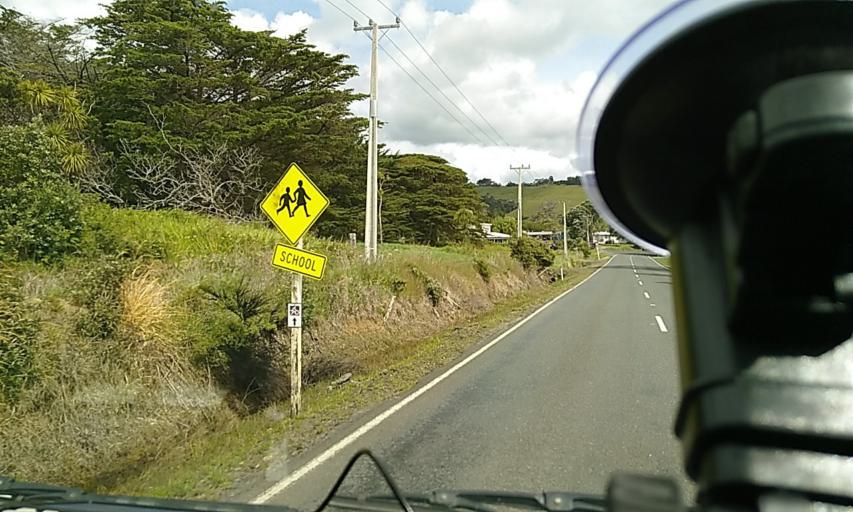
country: NZ
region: Northland
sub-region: Far North District
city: Ahipara
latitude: -35.5235
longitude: 173.3894
